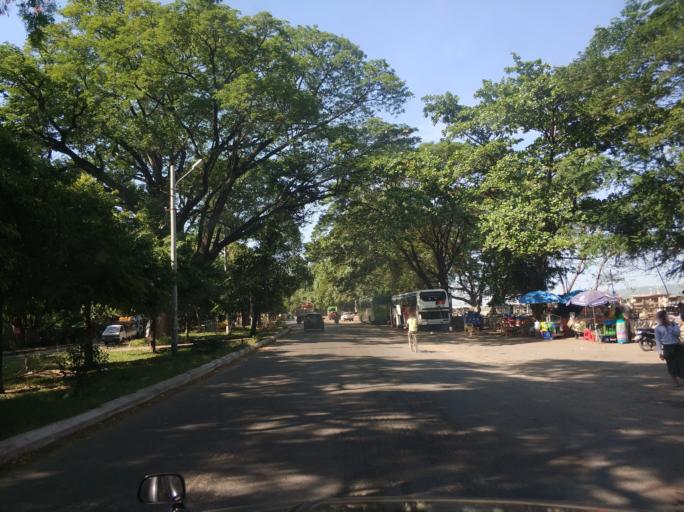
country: MM
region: Mandalay
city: Mandalay
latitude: 21.9712
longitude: 96.0566
